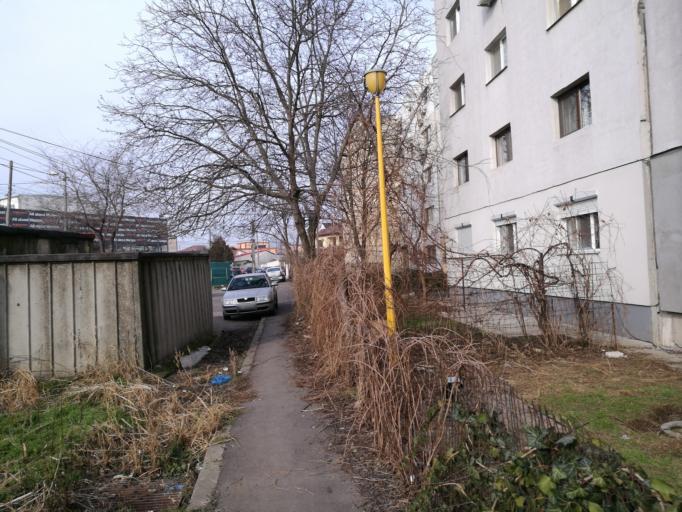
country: RO
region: Constanta
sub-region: Municipiul Constanta
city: Constanta
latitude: 44.1728
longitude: 28.6094
